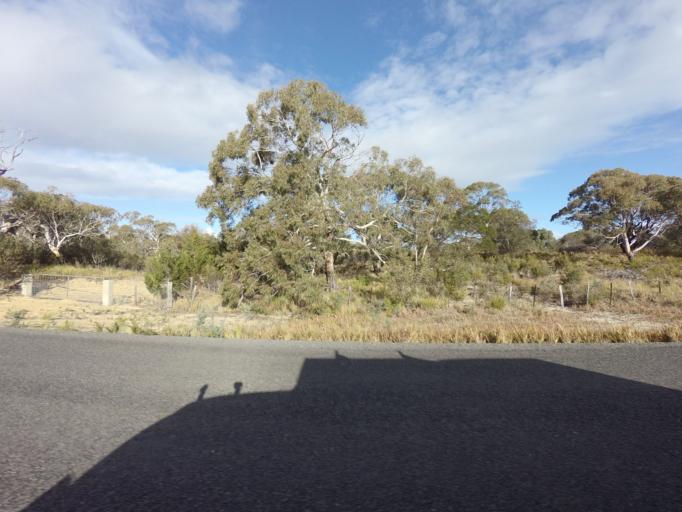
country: AU
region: Tasmania
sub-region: Break O'Day
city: St Helens
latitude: -42.0927
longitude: 148.2204
